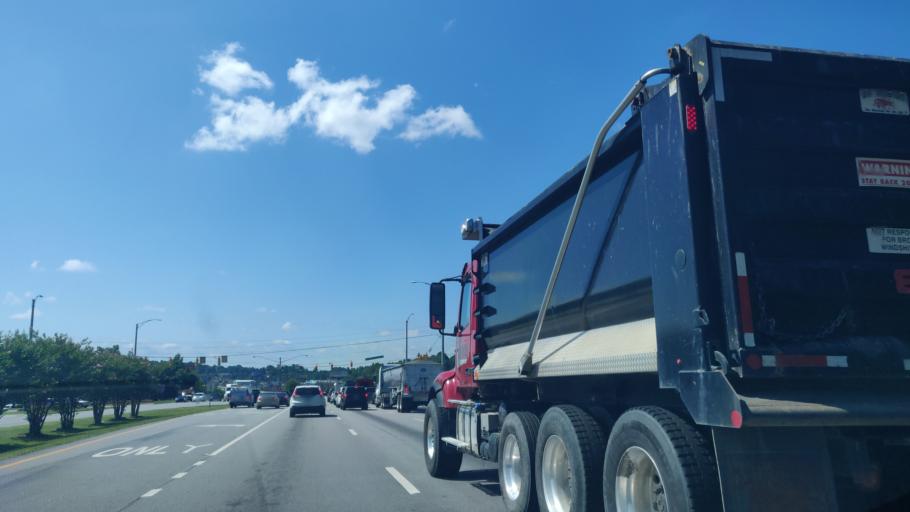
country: US
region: Alabama
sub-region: Russell County
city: Phenix City
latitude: 32.4763
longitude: -85.0303
